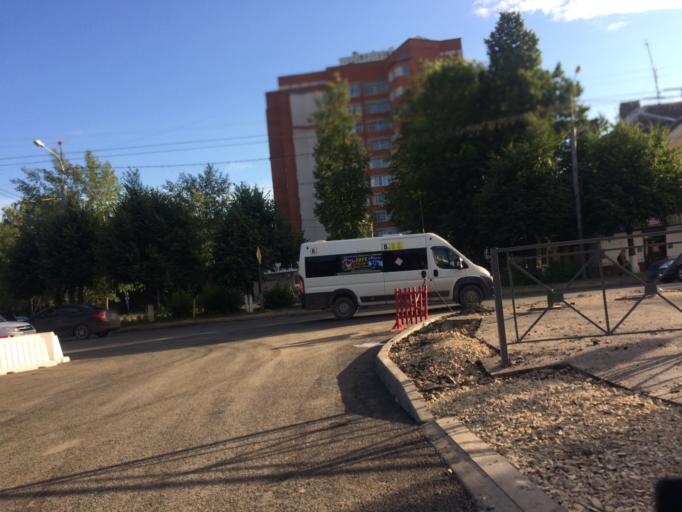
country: RU
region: Mariy-El
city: Yoshkar-Ola
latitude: 56.6333
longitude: 47.8790
